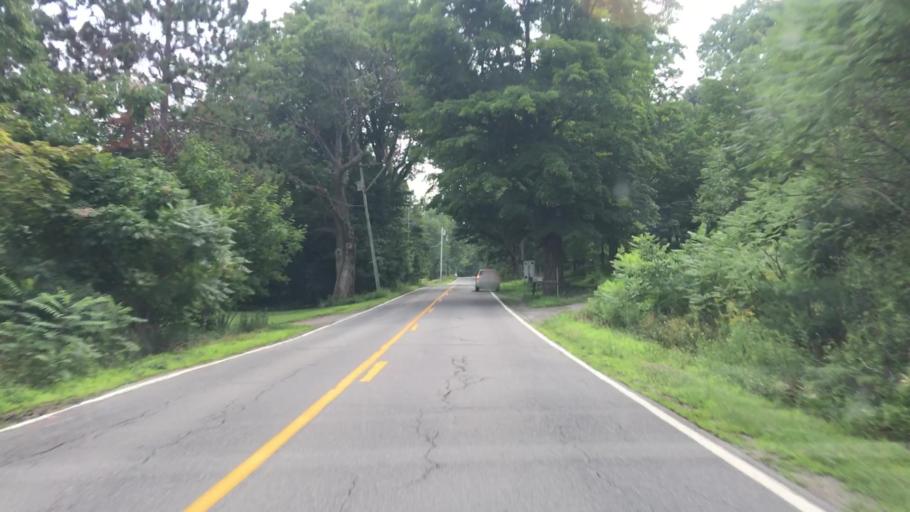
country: US
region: Maine
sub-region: Kennebec County
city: China
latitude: 44.4169
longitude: -69.5891
